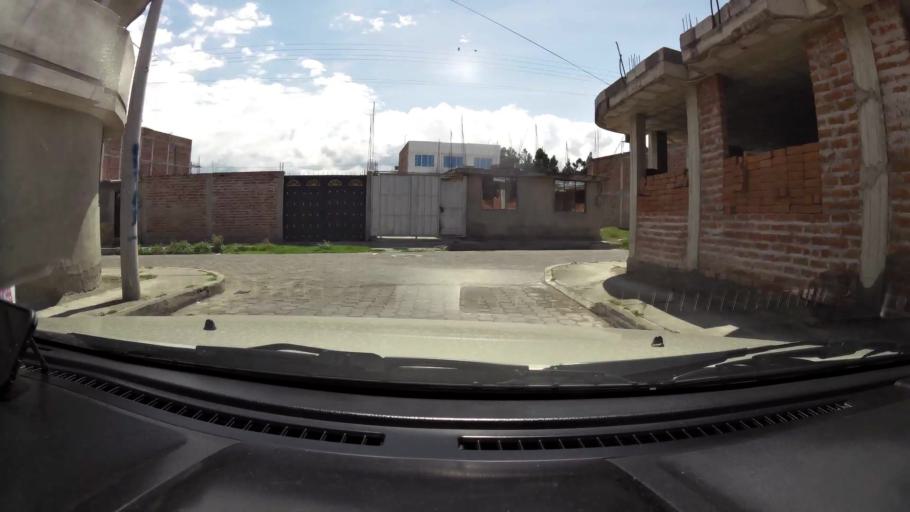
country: EC
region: Chimborazo
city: Riobamba
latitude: -1.6589
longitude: -78.6400
